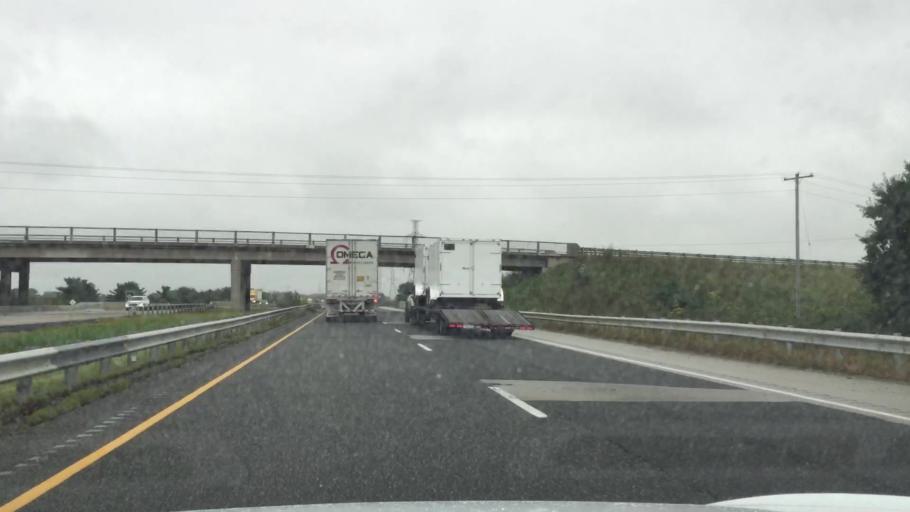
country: CA
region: Ontario
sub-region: Lambton County
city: Walpole Island
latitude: 42.3313
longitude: -82.2222
